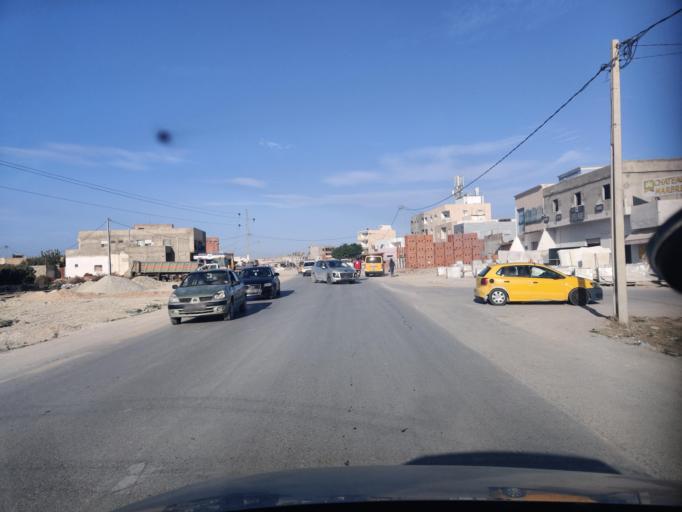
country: TN
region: Ariana
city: Ariana
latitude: 36.9570
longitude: 10.2071
